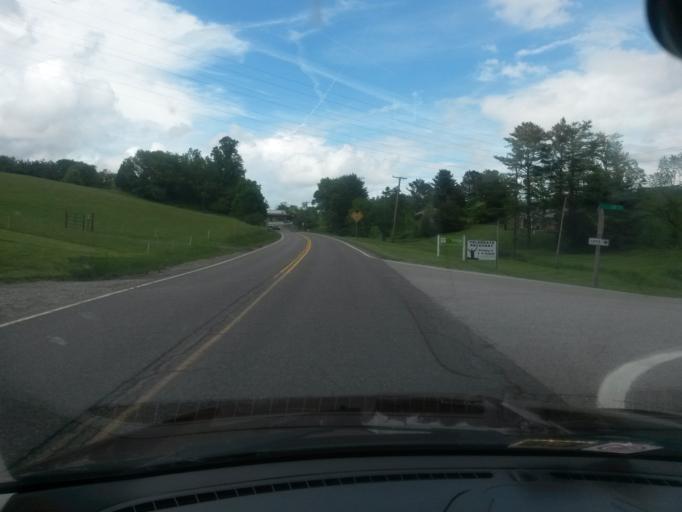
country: US
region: Virginia
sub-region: Montgomery County
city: Christiansburg
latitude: 37.1118
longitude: -80.4238
